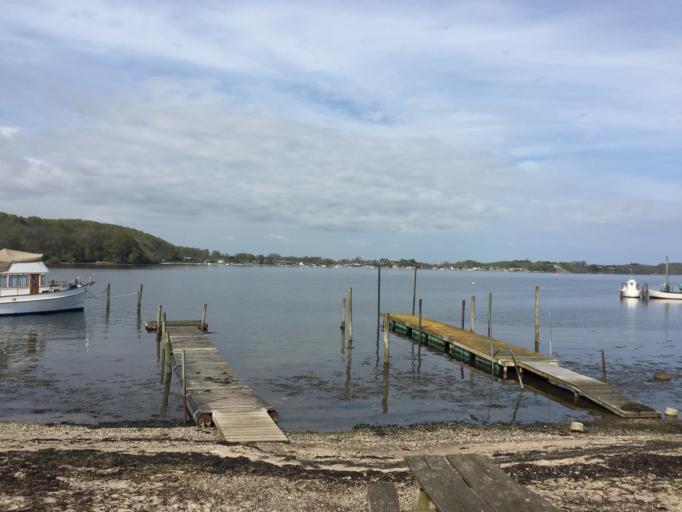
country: DK
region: South Denmark
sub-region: Aabenraa Kommune
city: Lojt Kirkeby
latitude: 55.1220
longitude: 9.4668
